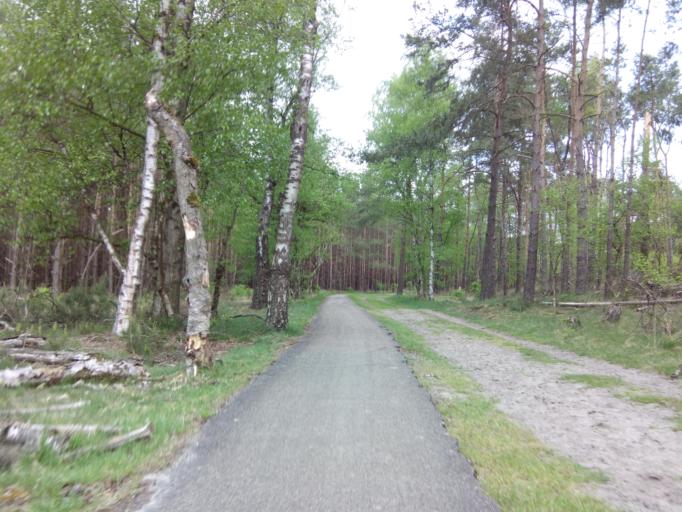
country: NL
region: Gelderland
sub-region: Gemeente Ede
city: Otterlo
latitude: 52.0794
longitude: 5.7605
